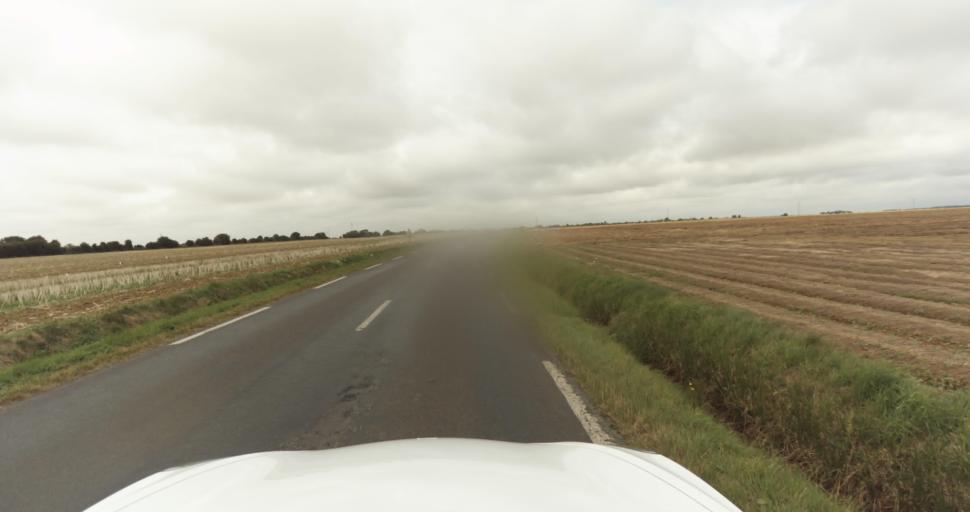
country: FR
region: Haute-Normandie
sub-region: Departement de l'Eure
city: Claville
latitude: 49.0770
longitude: 1.0606
